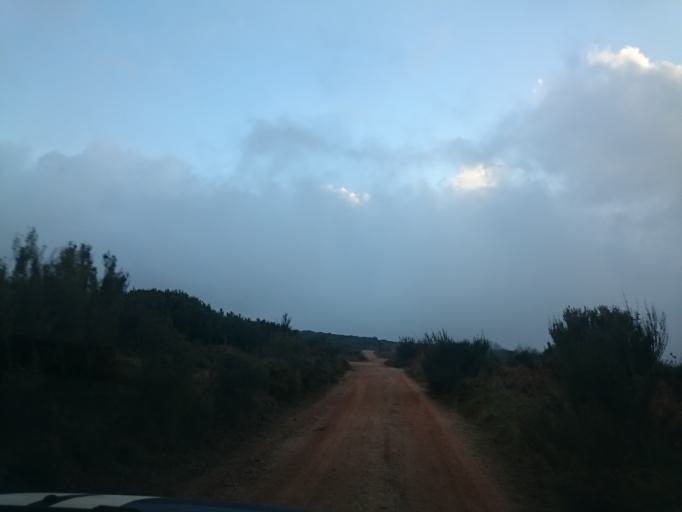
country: ES
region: Catalonia
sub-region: Provincia de Barcelona
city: Tagamanent
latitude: 41.7699
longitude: 2.3322
